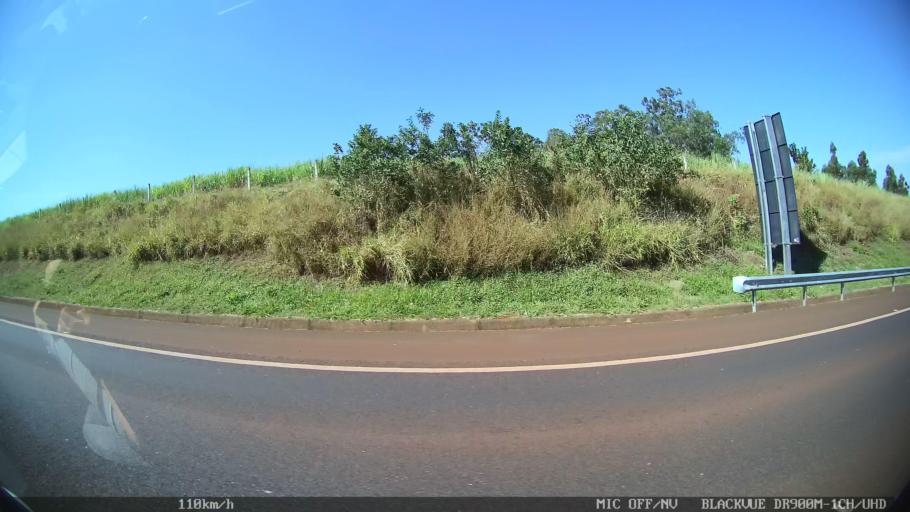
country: BR
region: Sao Paulo
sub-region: Franca
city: Franca
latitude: -20.6266
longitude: -47.4632
